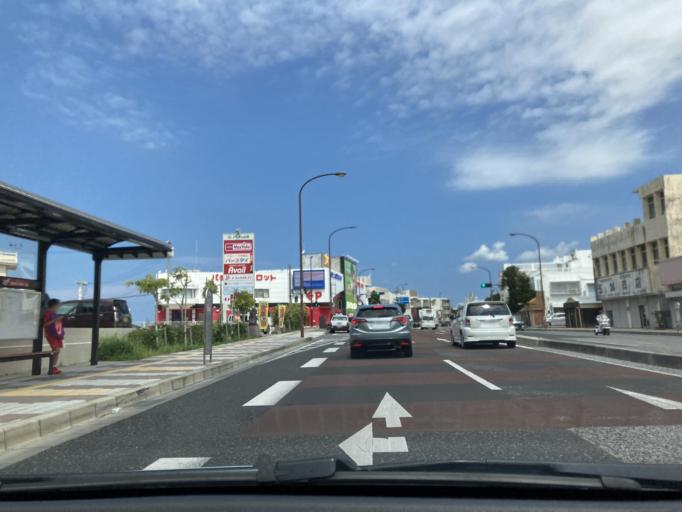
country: JP
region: Okinawa
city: Okinawa
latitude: 26.3240
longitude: 127.7930
